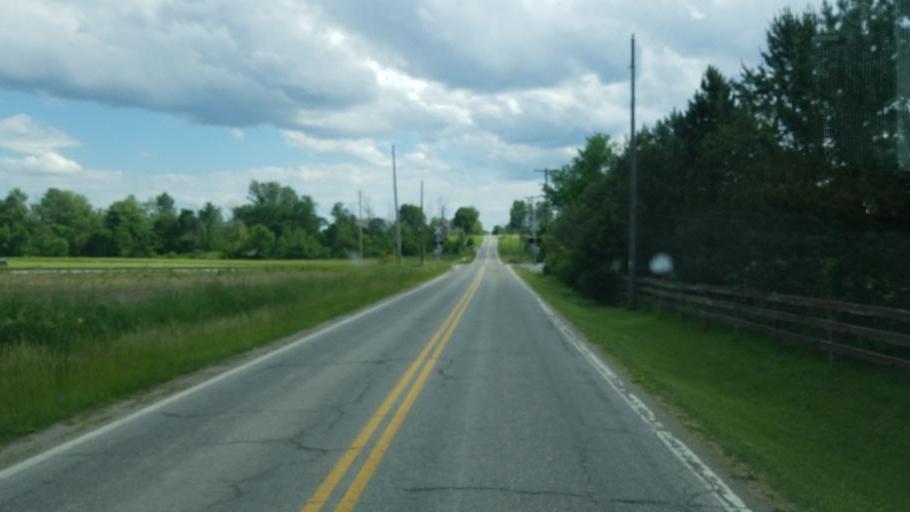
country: US
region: Ohio
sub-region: Huron County
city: Plymouth
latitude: 41.0117
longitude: -82.6069
